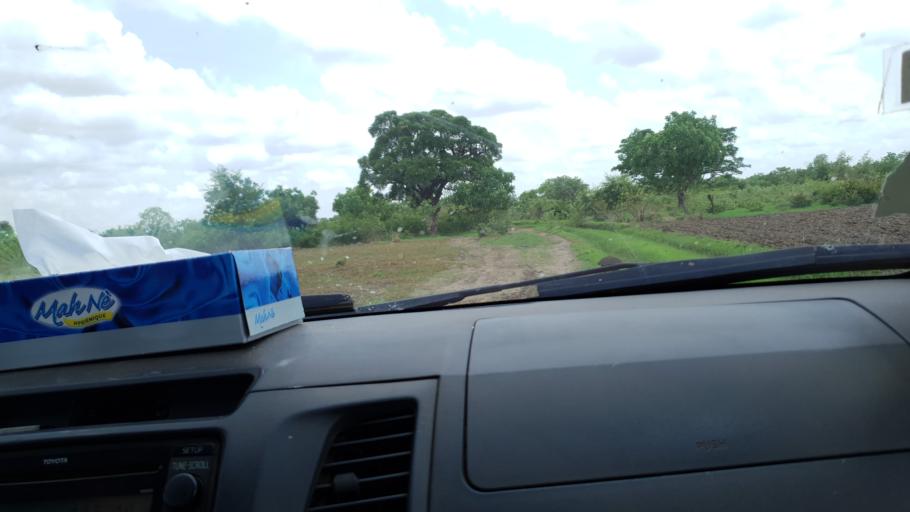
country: ML
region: Segou
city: Baroueli
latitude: 13.3468
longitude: -7.0939
